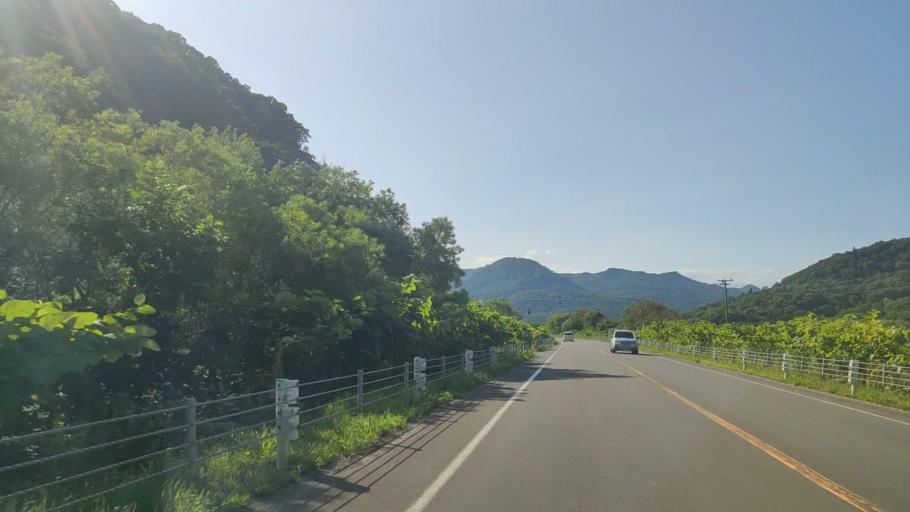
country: JP
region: Hokkaido
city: Nayoro
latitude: 44.7296
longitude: 142.2115
